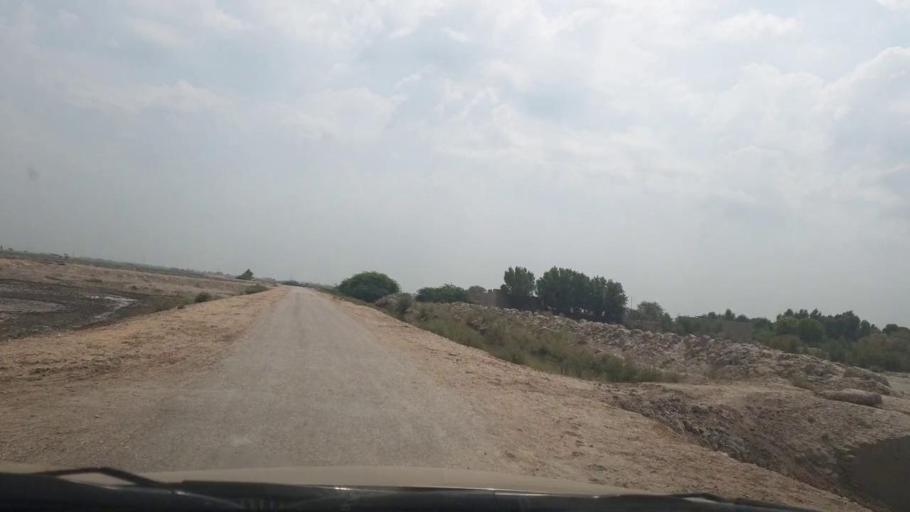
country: PK
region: Sindh
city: Ratodero
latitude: 27.6988
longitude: 68.2306
